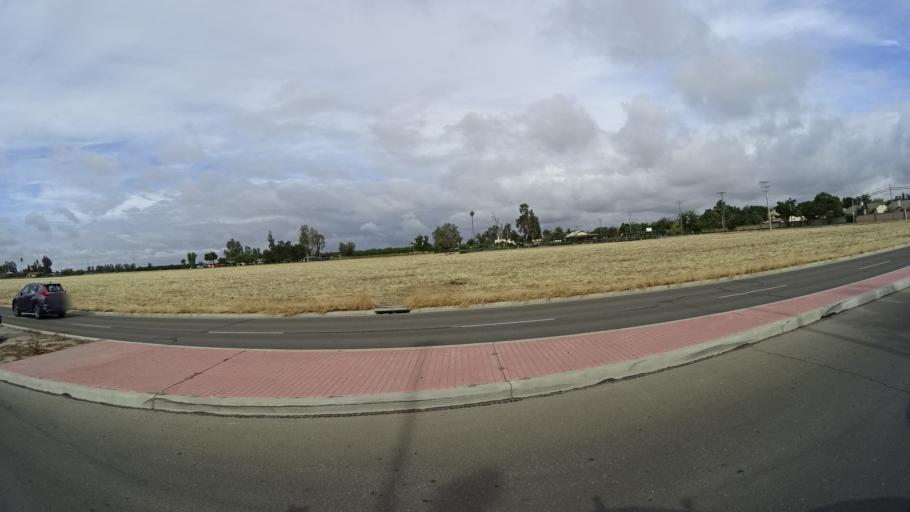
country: US
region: California
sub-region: Kings County
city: Armona
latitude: 36.3273
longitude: -119.6791
